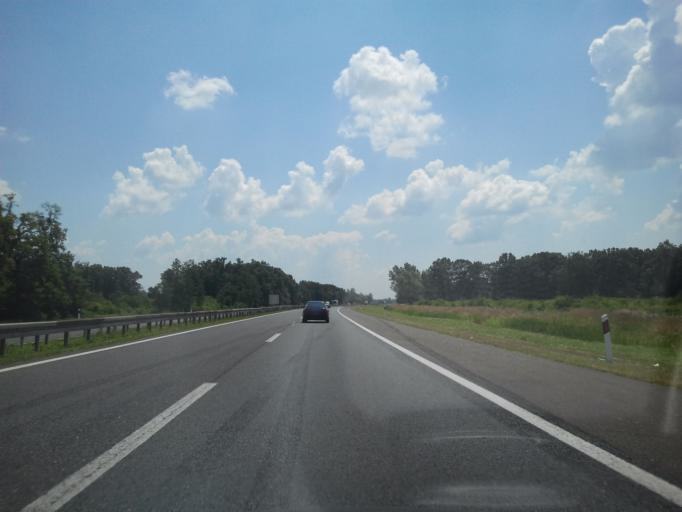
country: HR
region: Zagrebacka
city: Lupoglav
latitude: 45.7419
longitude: 16.3256
